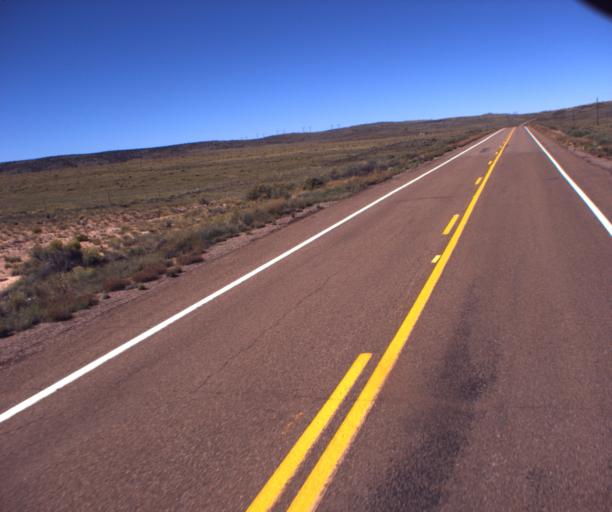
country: US
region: Arizona
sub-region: Apache County
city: Saint Johns
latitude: 34.5387
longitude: -109.4687
